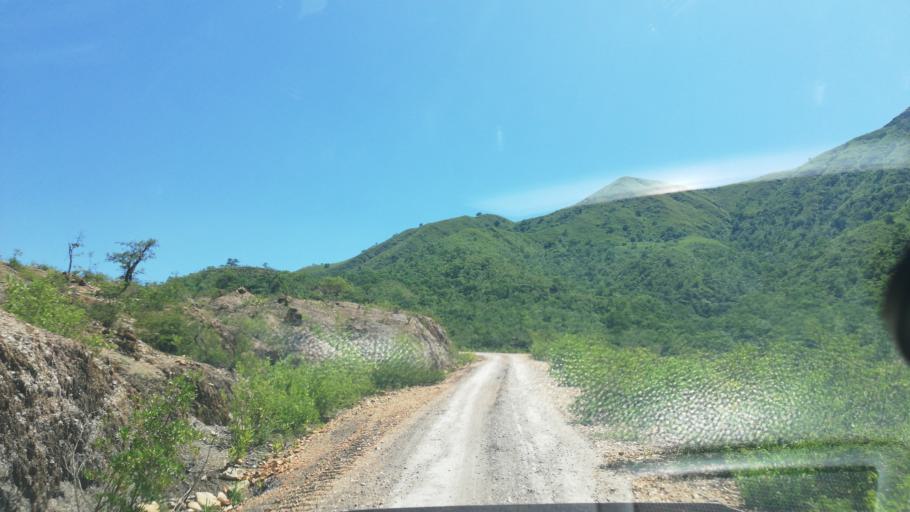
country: BO
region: Cochabamba
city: Mizque
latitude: -17.8797
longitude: -65.2888
